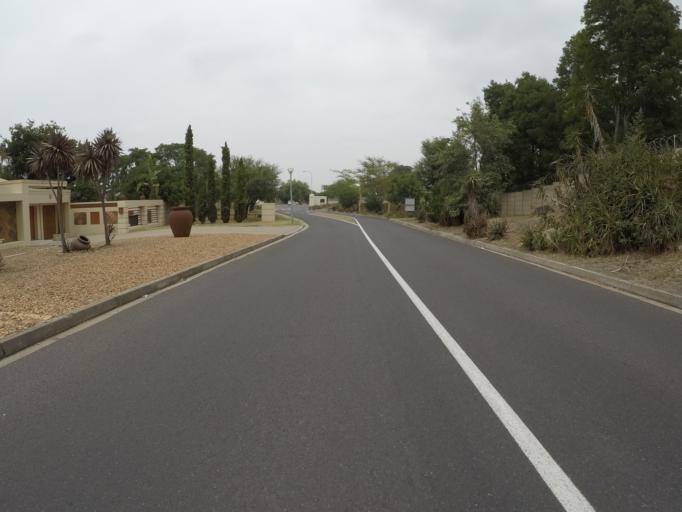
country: ZA
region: Western Cape
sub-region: City of Cape Town
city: Kraaifontein
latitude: -33.8711
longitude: 18.6447
